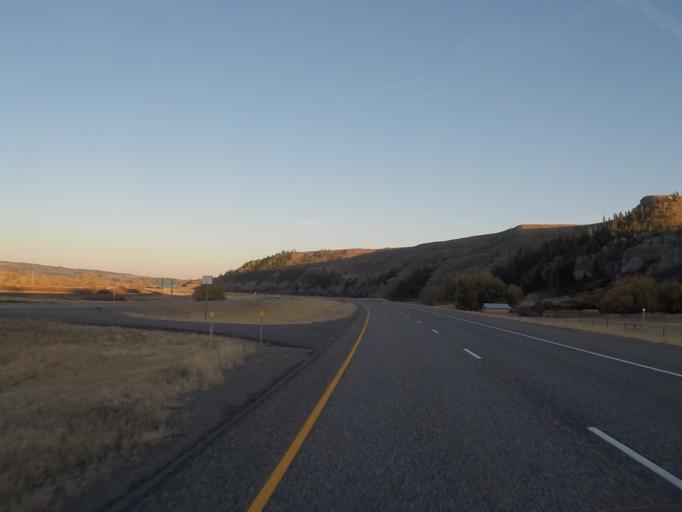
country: US
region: Montana
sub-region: Sweet Grass County
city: Big Timber
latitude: 45.7325
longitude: -109.7498
